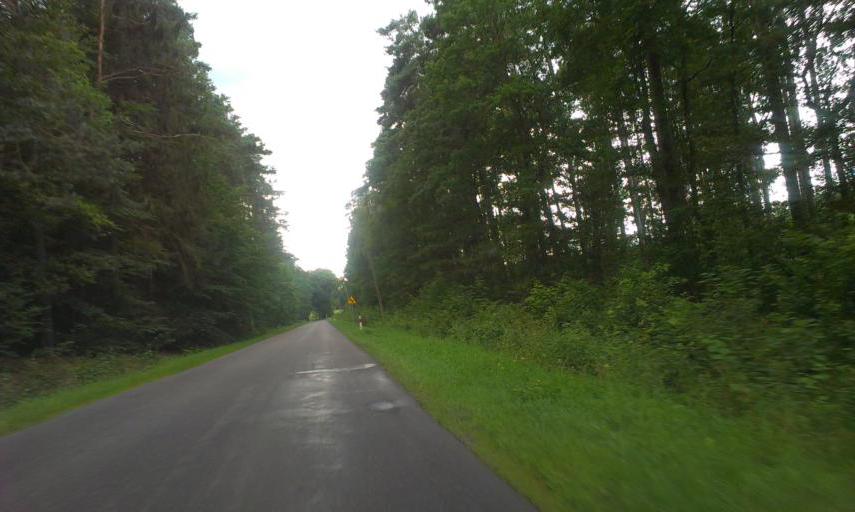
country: PL
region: West Pomeranian Voivodeship
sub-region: Powiat bialogardzki
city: Tychowo
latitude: 53.8717
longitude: 16.1751
